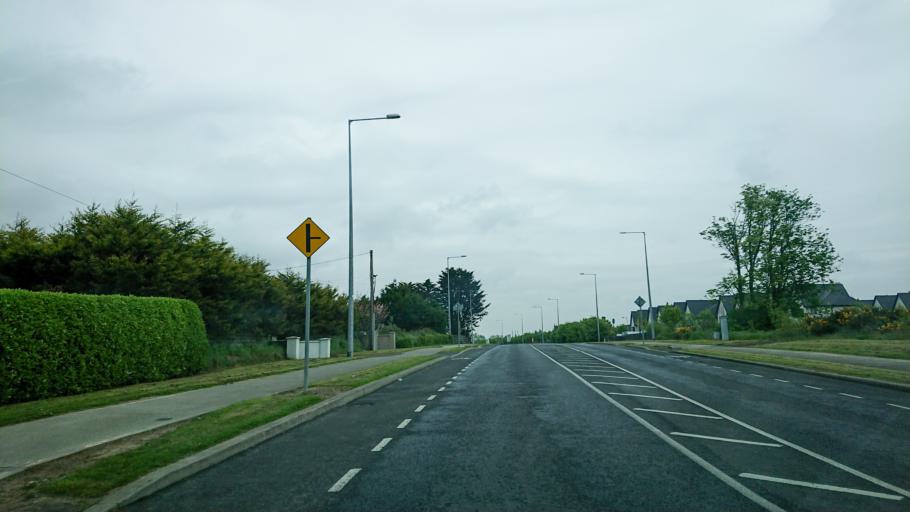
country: IE
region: Munster
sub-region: Waterford
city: Waterford
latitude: 52.2332
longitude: -7.1417
